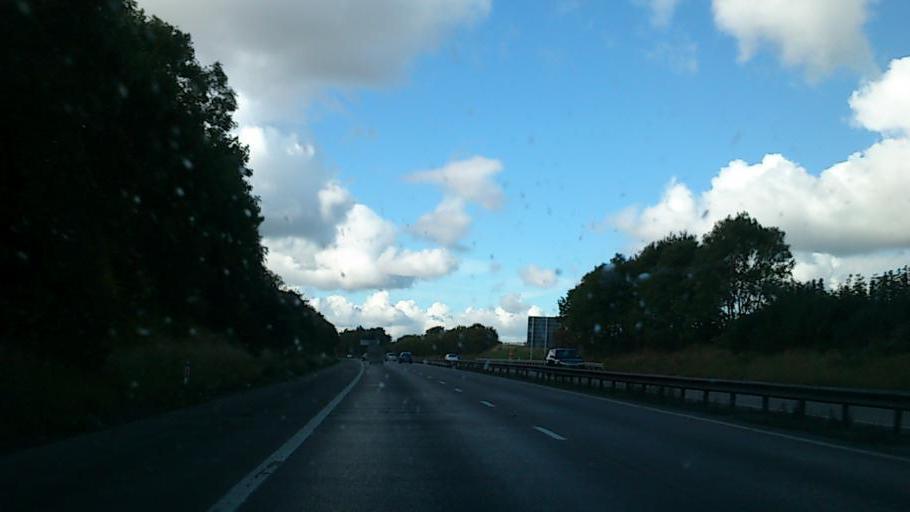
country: GB
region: England
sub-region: Staffordshire
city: Brewood
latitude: 52.6427
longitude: -2.1682
